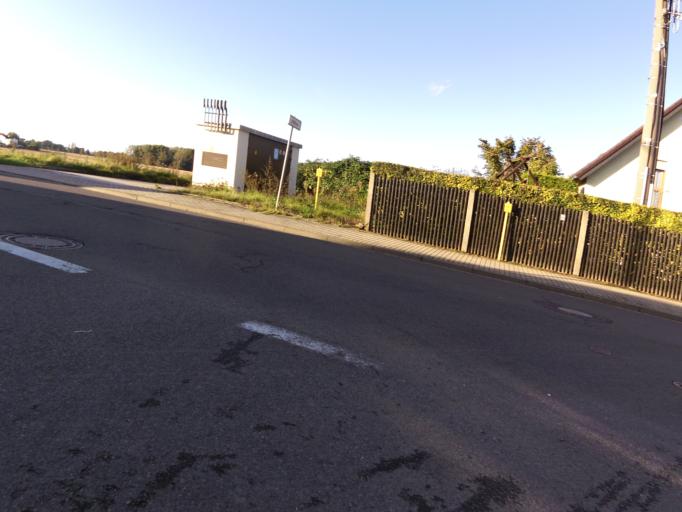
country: DE
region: Saxony
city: Taucha
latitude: 51.3238
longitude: 12.4716
